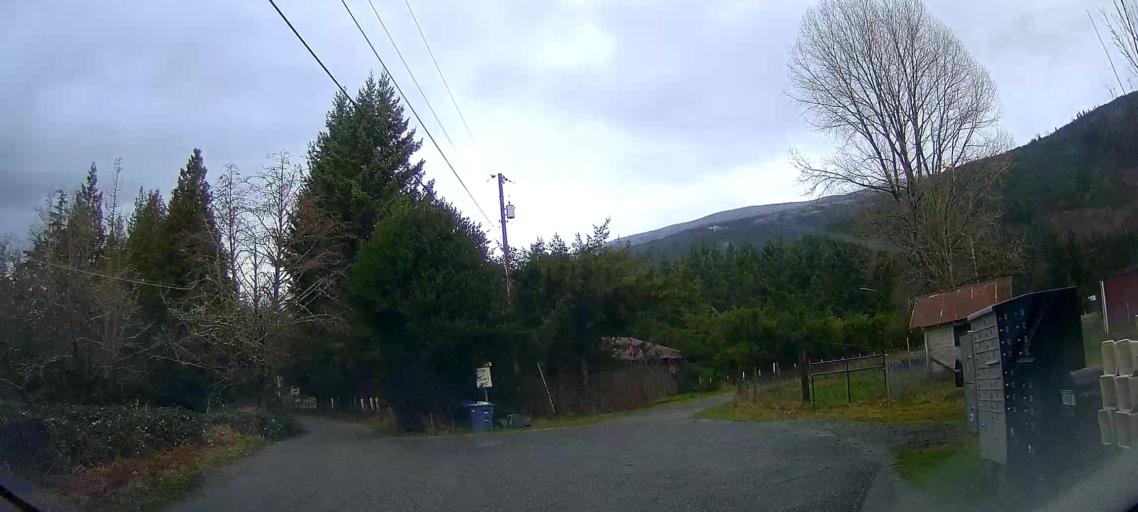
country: US
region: Washington
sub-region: Skagit County
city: Sedro-Woolley
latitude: 48.5910
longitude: -122.2232
